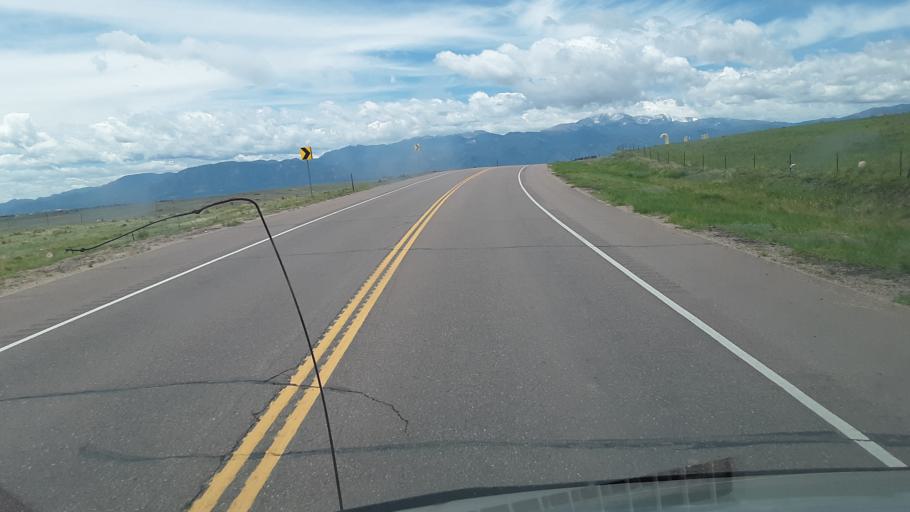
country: US
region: Colorado
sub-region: El Paso County
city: Cimarron Hills
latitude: 38.8350
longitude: -104.6422
